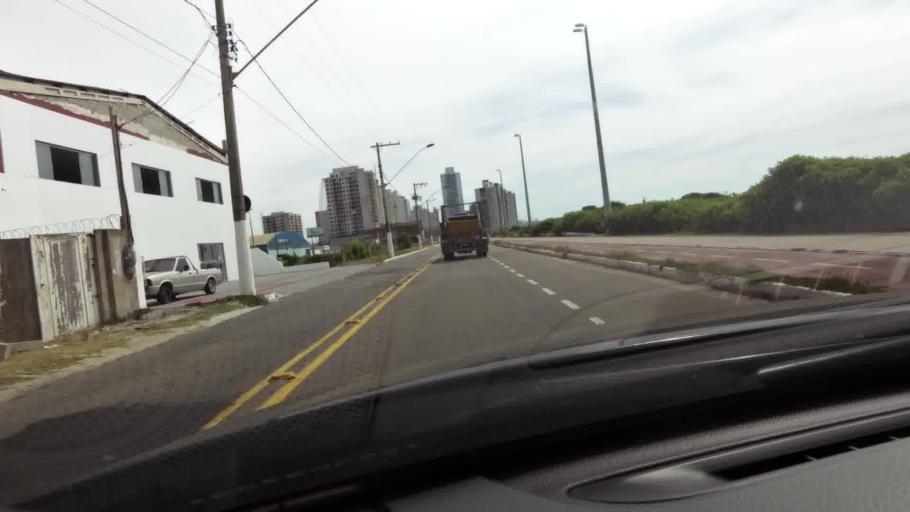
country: BR
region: Espirito Santo
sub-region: Vila Velha
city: Vila Velha
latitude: -20.3833
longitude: -40.3102
